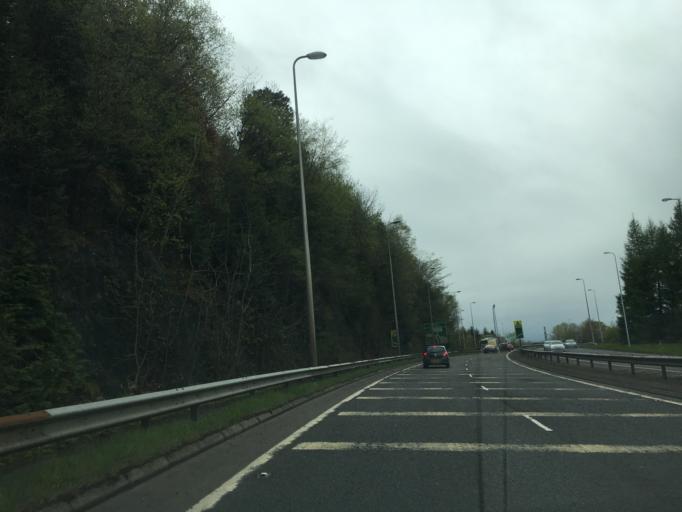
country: GB
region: Scotland
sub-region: Inverclyde
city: Kilmacolm
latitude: 55.9293
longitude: -4.6405
